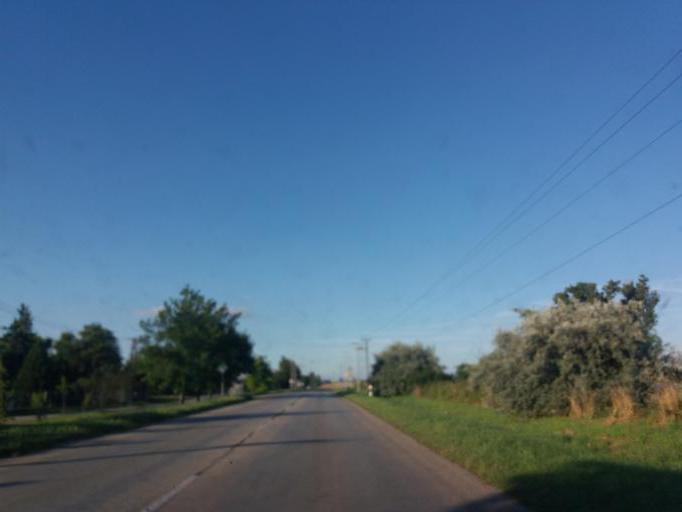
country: HU
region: Fejer
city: Baracska
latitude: 47.2629
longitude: 18.7203
